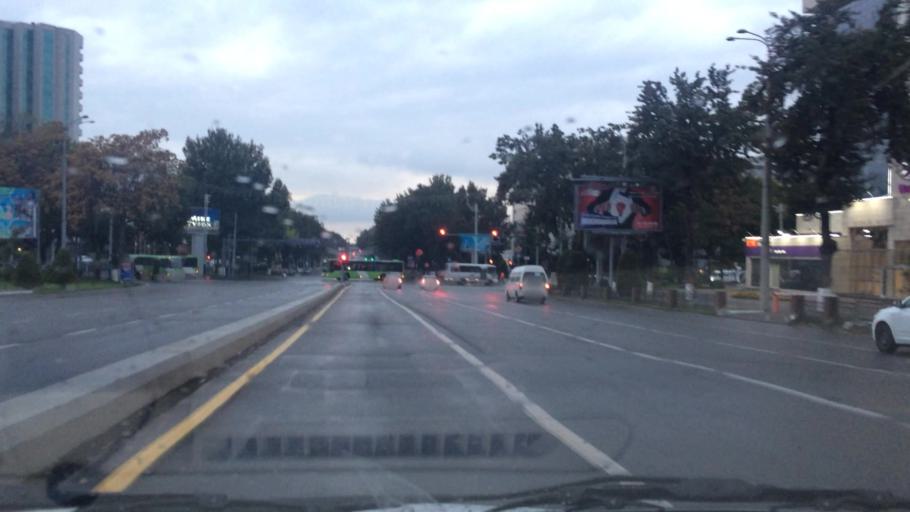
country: UZ
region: Toshkent Shahri
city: Tashkent
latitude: 41.3164
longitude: 69.2824
